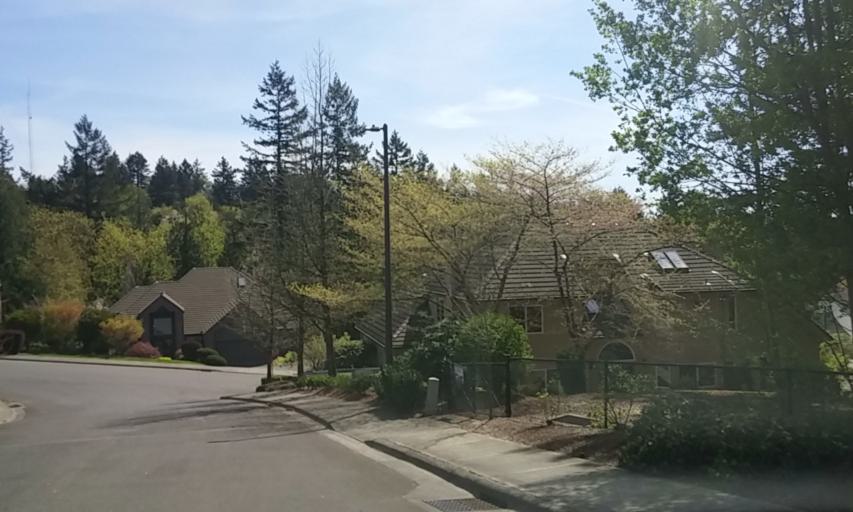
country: US
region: Oregon
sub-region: Washington County
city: West Haven-Sylvan
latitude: 45.5137
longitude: -122.7469
